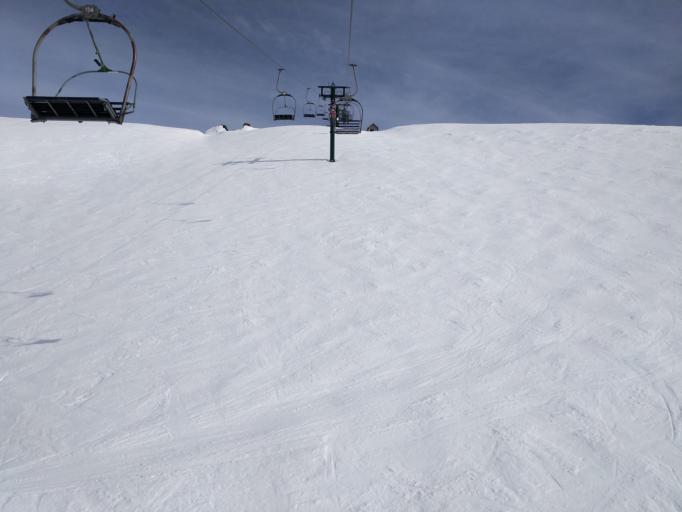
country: AR
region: Rio Negro
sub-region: Departamento de Bariloche
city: San Carlos de Bariloche
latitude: -41.1586
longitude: -71.4743
